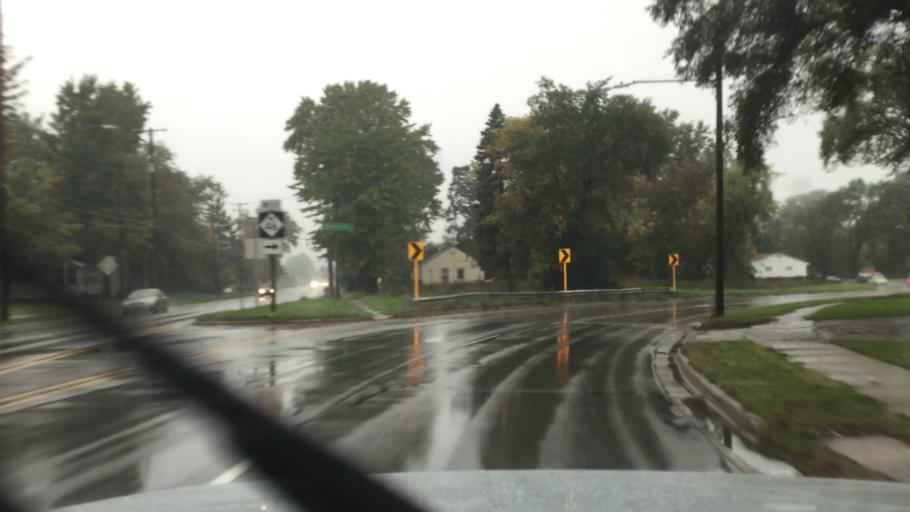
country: US
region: Michigan
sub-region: Saginaw County
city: Buena Vista
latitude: 43.4148
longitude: -83.9146
